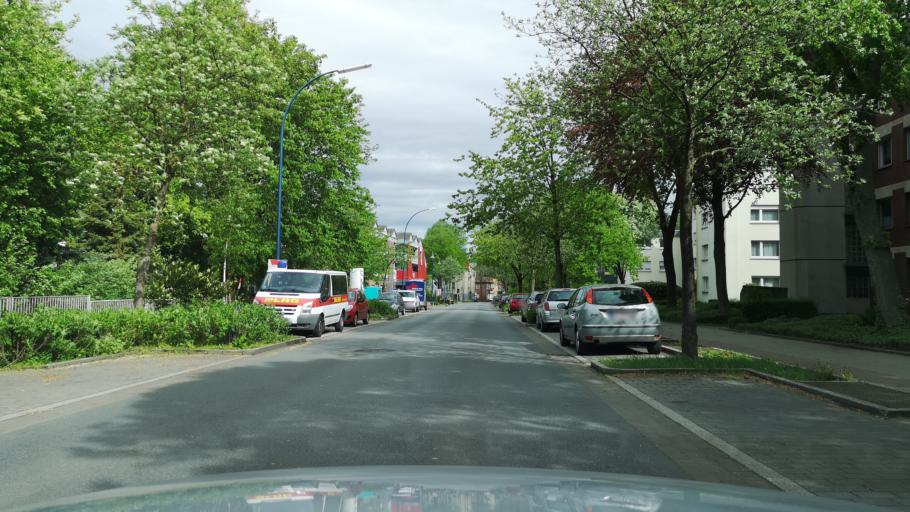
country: DE
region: North Rhine-Westphalia
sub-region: Regierungsbezirk Arnsberg
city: Holzwickede
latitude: 51.4974
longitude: 7.6162
